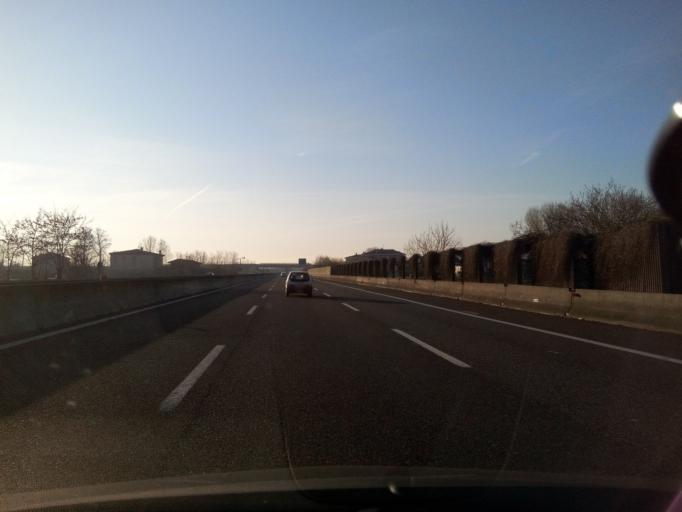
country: IT
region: Lombardy
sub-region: Provincia di Lodi
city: Guardamiglio
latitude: 45.1144
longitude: 9.6815
